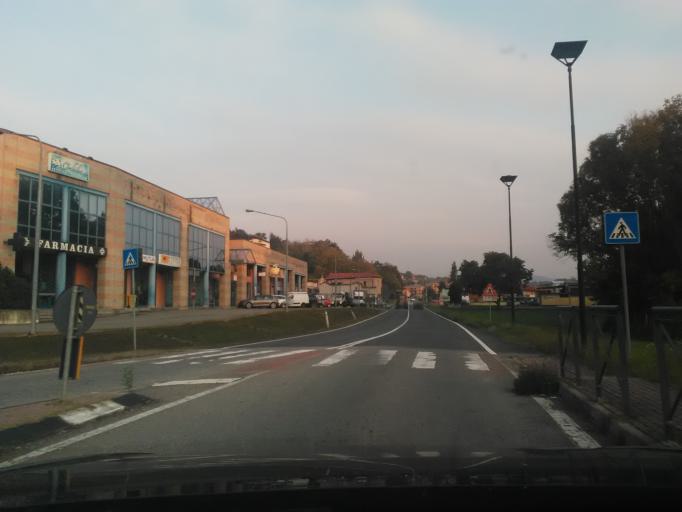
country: IT
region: Piedmont
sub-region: Provincia di Vercelli
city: San Maurizio
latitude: 45.5994
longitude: 8.2917
